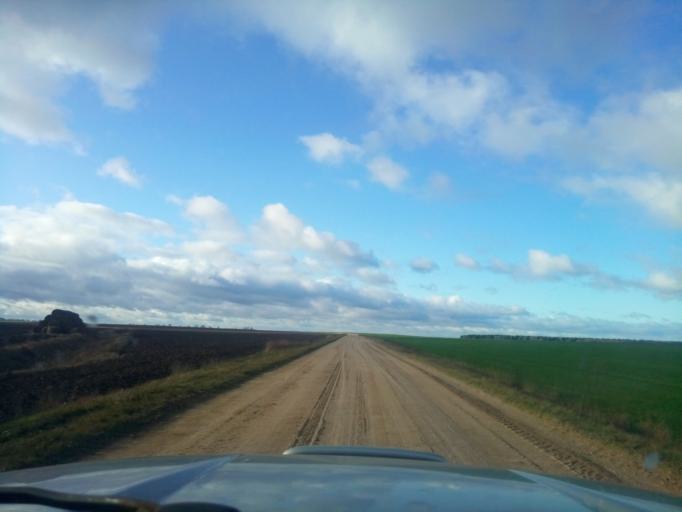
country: BY
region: Minsk
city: Tsimkavichy
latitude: 53.1965
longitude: 26.9196
